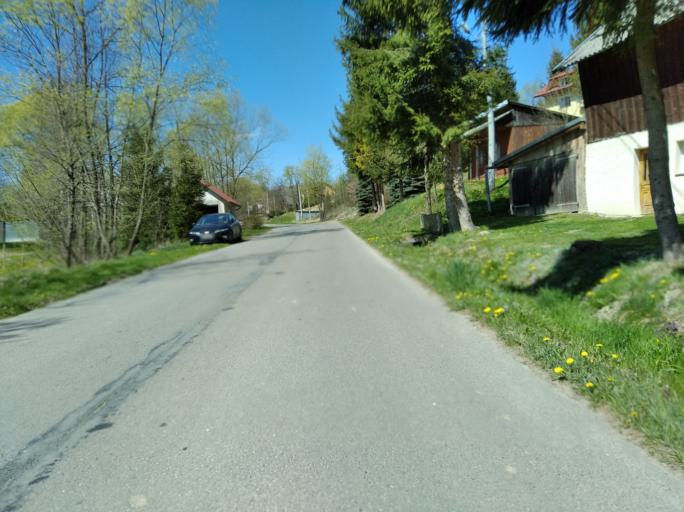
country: PL
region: Subcarpathian Voivodeship
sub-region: Powiat brzozowski
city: Jablonka
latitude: 49.7216
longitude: 22.1194
